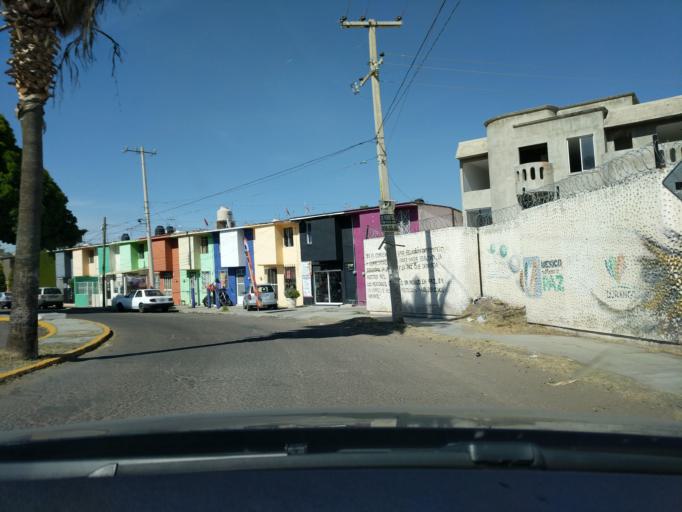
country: MX
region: Durango
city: Victoria de Durango
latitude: 24.0057
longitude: -104.6545
